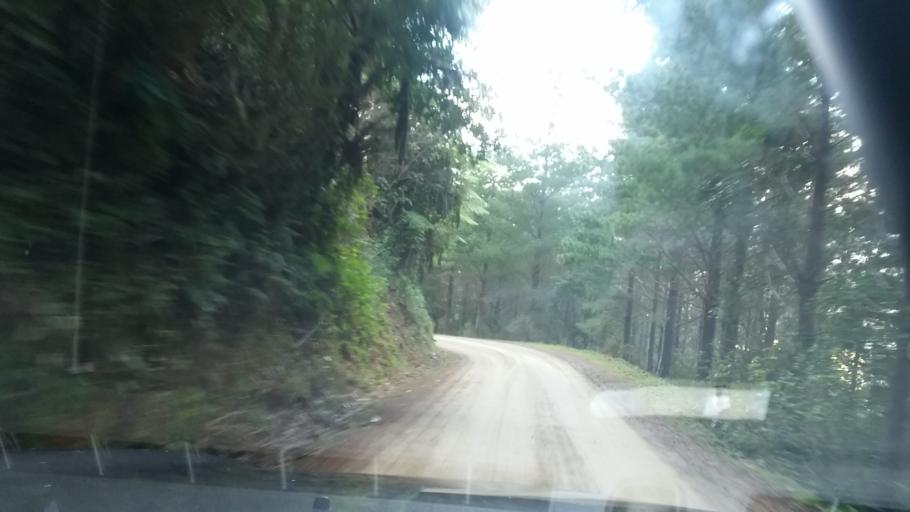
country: NZ
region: Marlborough
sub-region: Marlborough District
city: Picton
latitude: -40.9849
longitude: 173.8195
